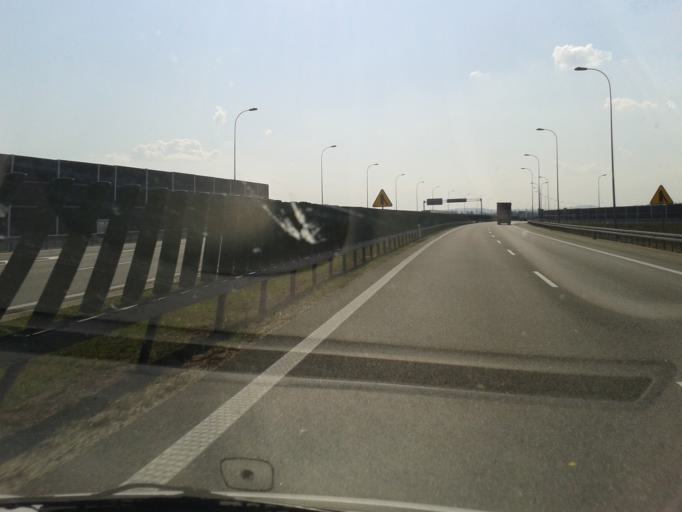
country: PL
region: Lesser Poland Voivodeship
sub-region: Powiat tarnowski
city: Wierzchoslawice
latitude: 50.0139
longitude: 20.8679
